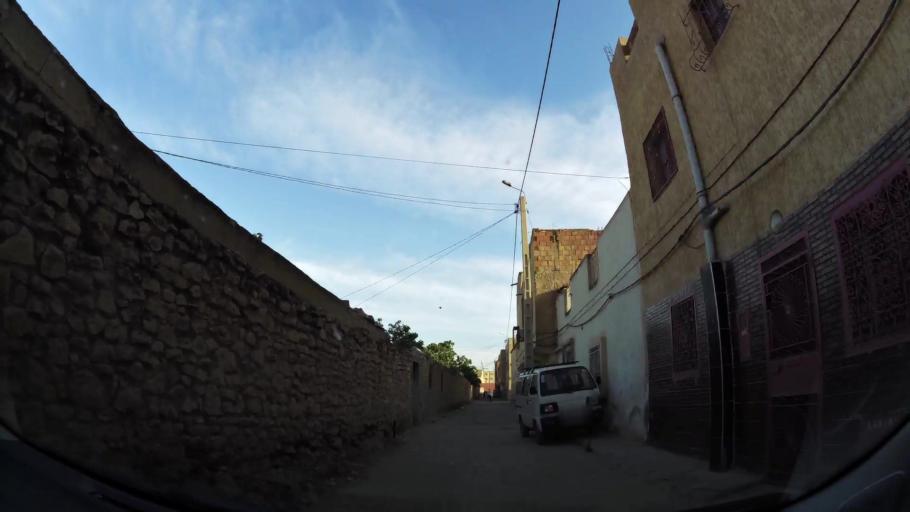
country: MA
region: Oriental
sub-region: Oujda-Angad
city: Oujda
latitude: 34.7014
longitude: -1.9048
